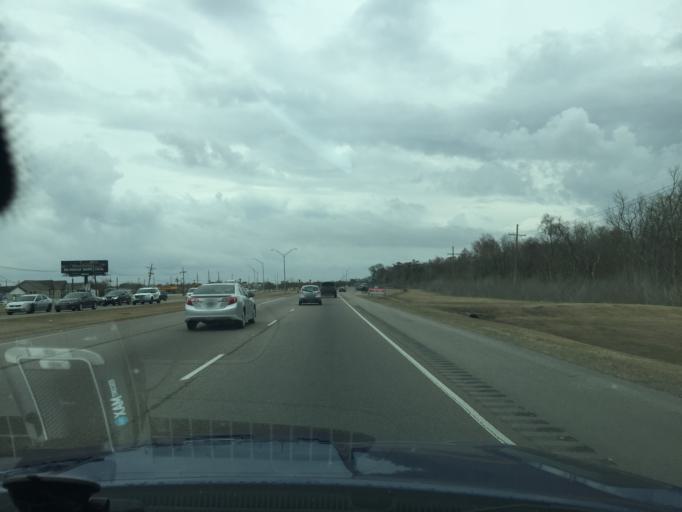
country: US
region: Louisiana
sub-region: Jefferson Parish
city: Westwego
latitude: 29.9063
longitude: -90.1597
